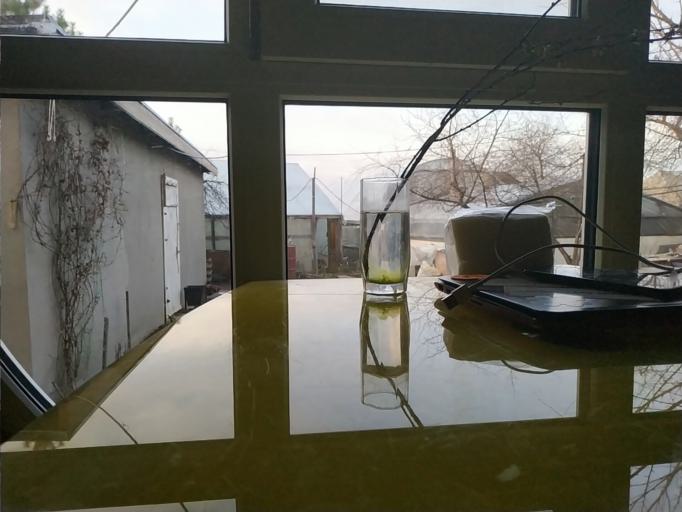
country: RU
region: Republic of Karelia
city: Suoyarvi
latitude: 62.3898
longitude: 32.0315
